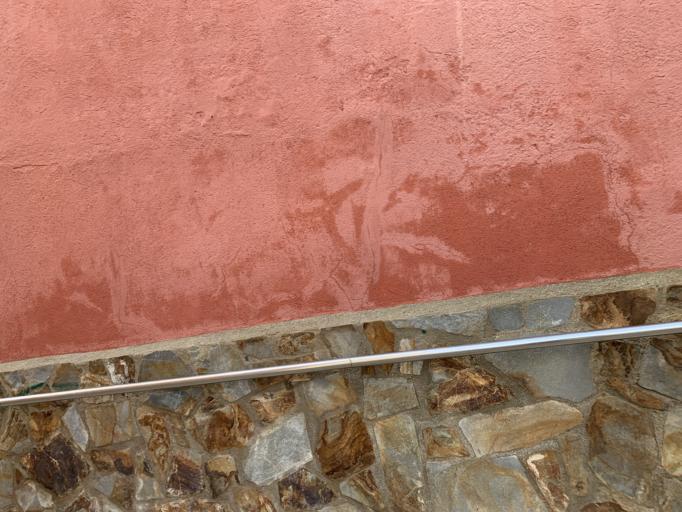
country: ES
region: Catalonia
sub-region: Provincia de Barcelona
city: El Masnou
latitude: 41.4777
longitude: 2.3116
